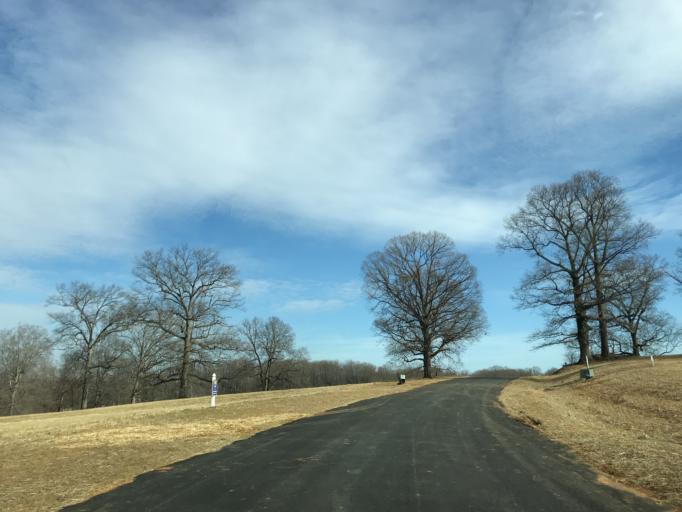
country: US
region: Maryland
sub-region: Baltimore County
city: Kingsville
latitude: 39.4526
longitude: -76.4076
